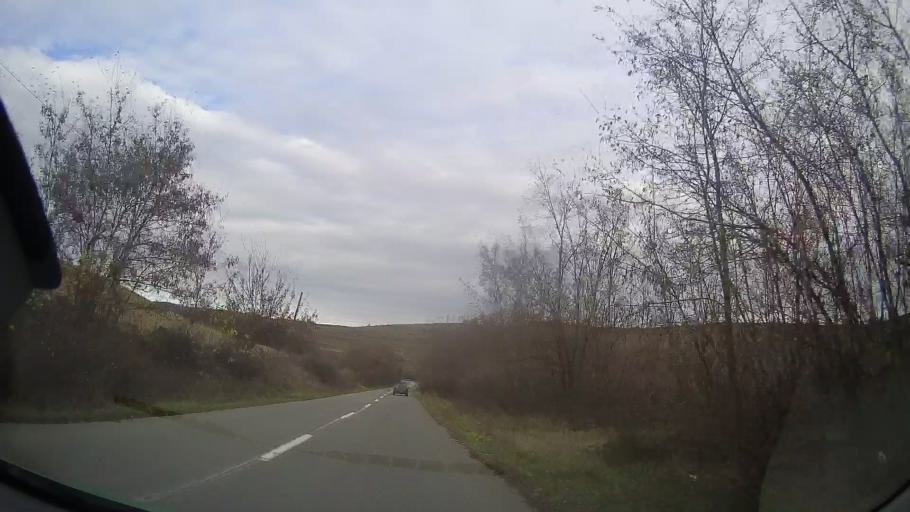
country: RO
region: Bistrita-Nasaud
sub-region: Comuna Milas
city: Milas
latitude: 46.8342
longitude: 24.4475
